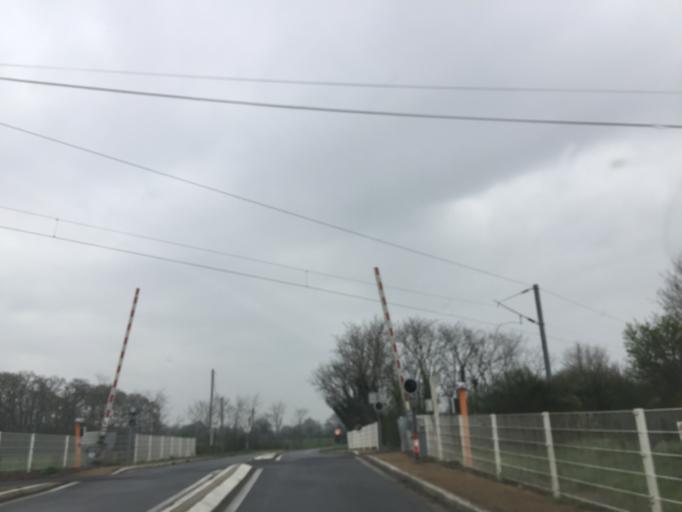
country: FR
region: Pays de la Loire
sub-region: Departement de la Loire-Atlantique
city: Casson
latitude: 47.3957
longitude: -1.5269
